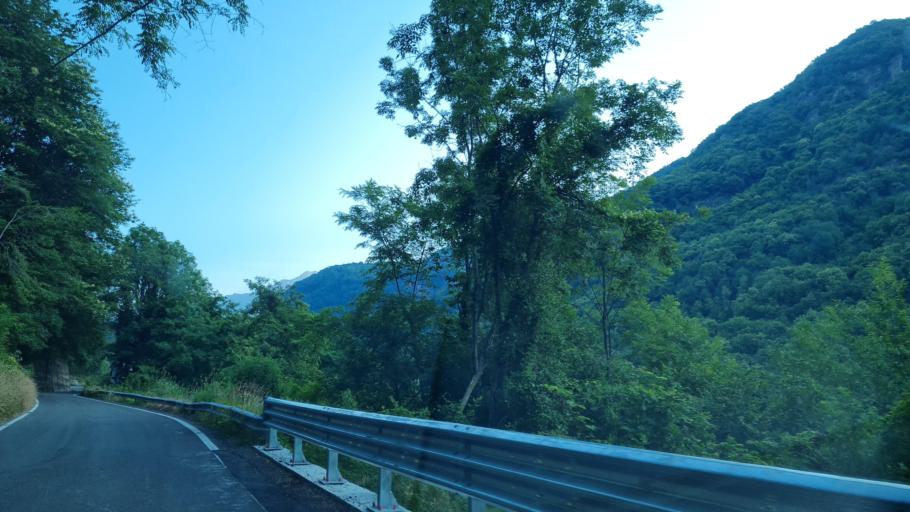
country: IT
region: Piedmont
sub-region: Provincia di Torino
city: Pont-Canavese
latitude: 45.4315
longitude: 7.5897
